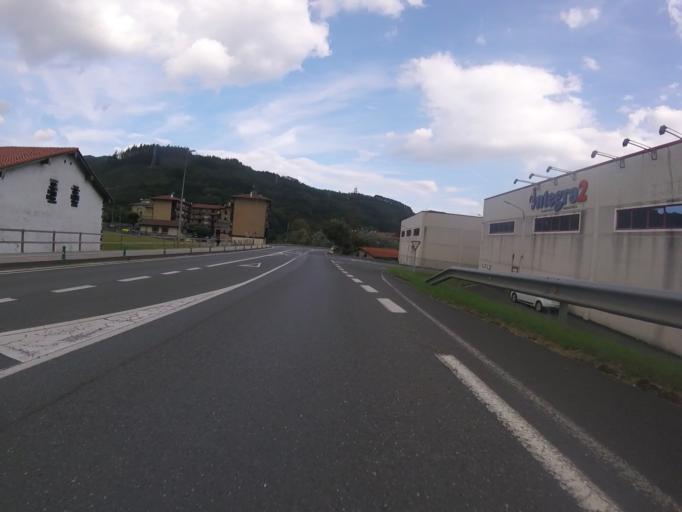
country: ES
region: Basque Country
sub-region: Provincia de Guipuzcoa
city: Anoeta
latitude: 43.1627
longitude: -2.0694
